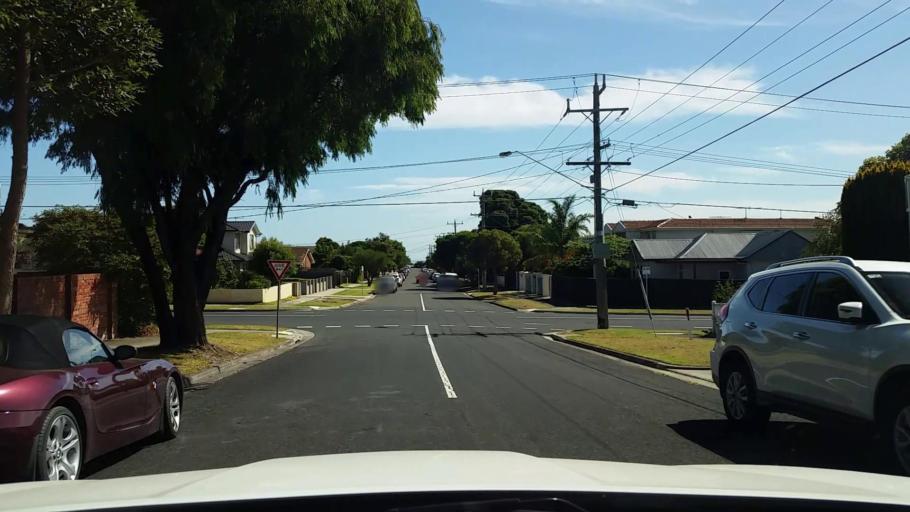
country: AU
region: Victoria
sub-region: Frankston
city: Frankston
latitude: -38.1498
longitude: 145.1205
